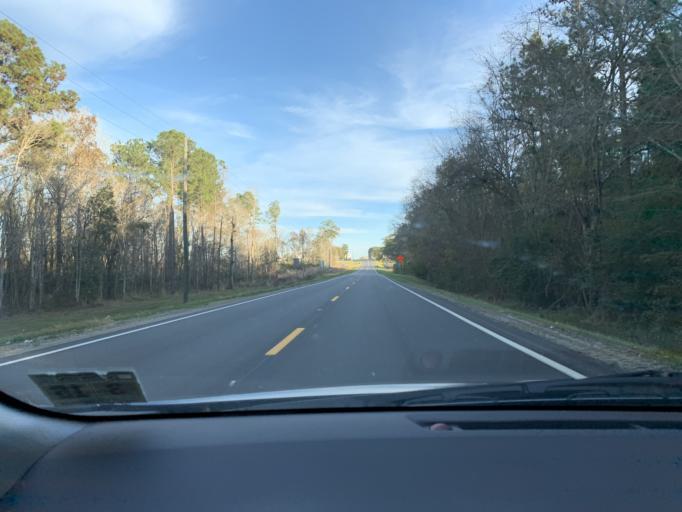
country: US
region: Georgia
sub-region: Coffee County
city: Broxton
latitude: 31.5803
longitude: -83.0609
